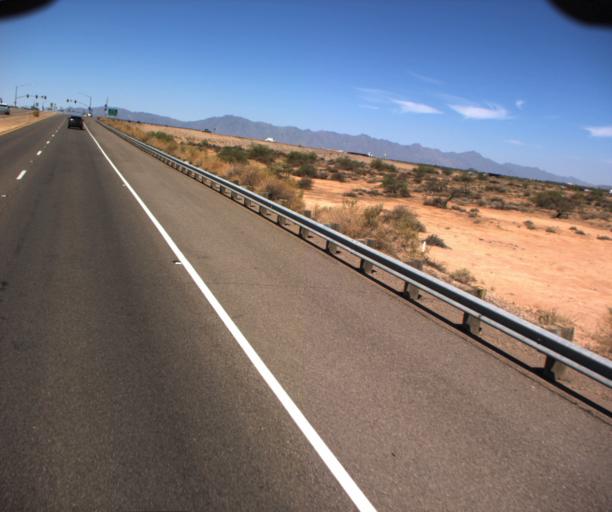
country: US
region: Arizona
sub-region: Maricopa County
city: Sun Lakes
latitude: 33.2577
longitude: -111.9444
